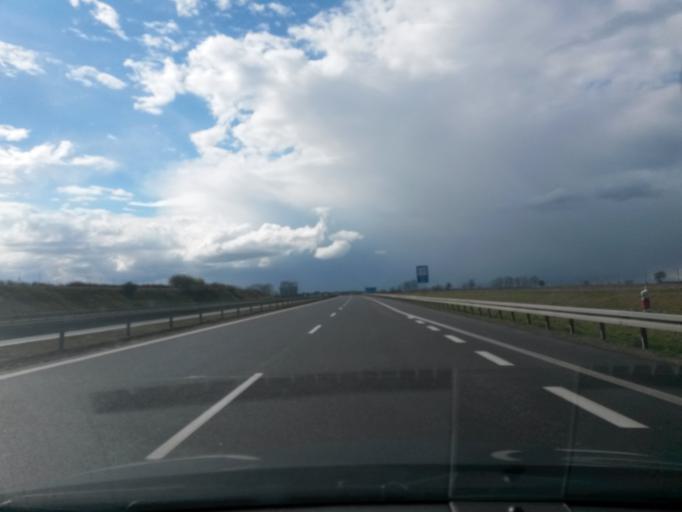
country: PL
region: Greater Poland Voivodeship
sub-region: Powiat wrzesinski
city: Wrzesnia
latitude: 52.3162
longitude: 17.5289
